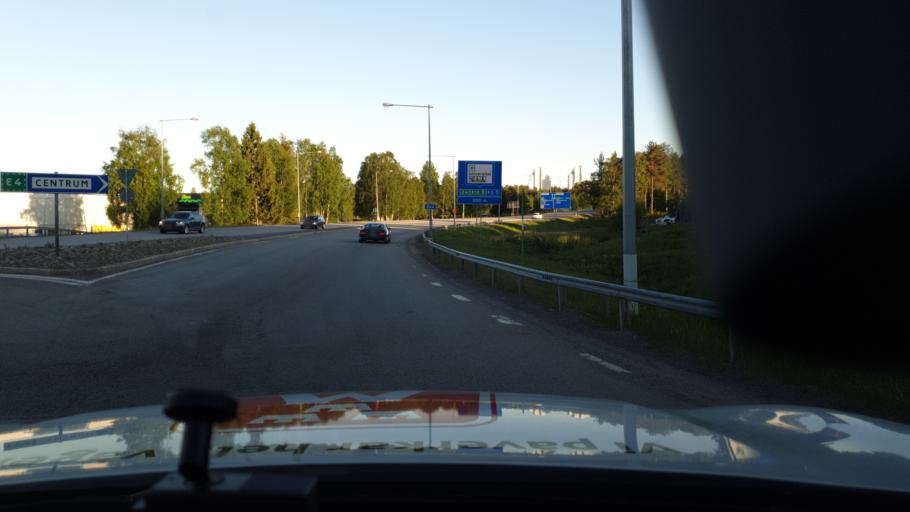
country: SE
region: Vaesterbotten
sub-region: Umea Kommun
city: Ersmark
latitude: 63.8530
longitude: 20.2971
